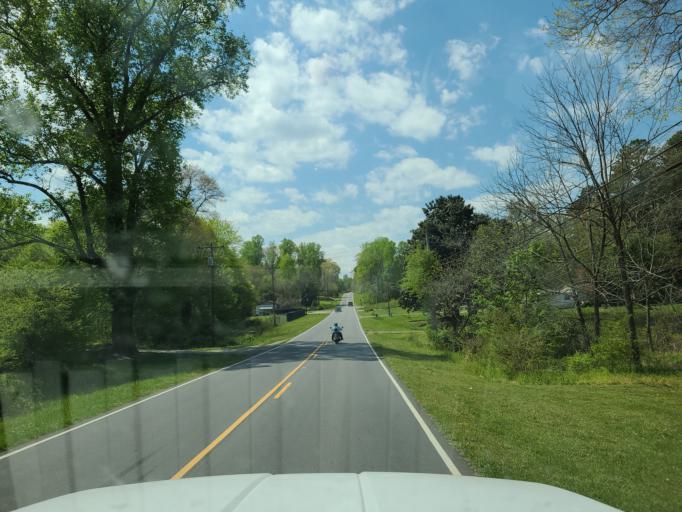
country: US
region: North Carolina
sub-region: Lincoln County
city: Lincolnton
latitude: 35.4556
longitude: -81.2746
